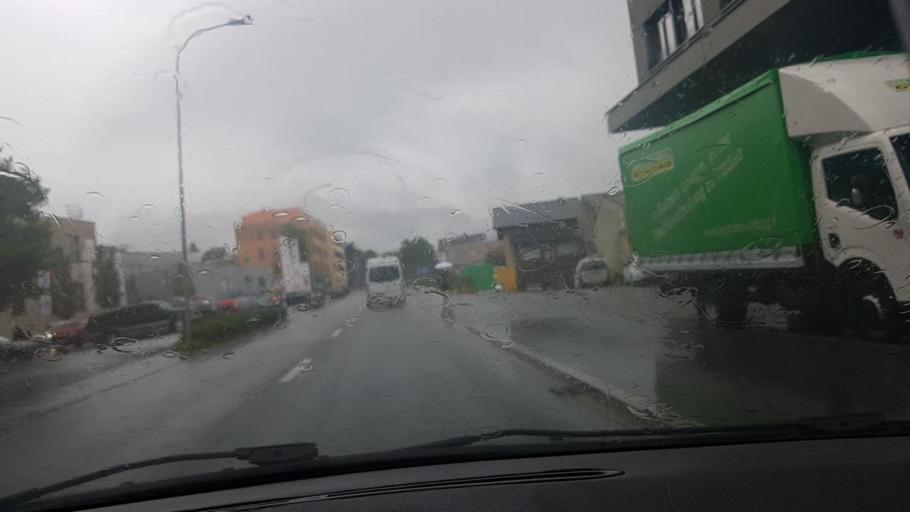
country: LI
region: Balzers
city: Balzers
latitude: 47.0763
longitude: 9.5123
